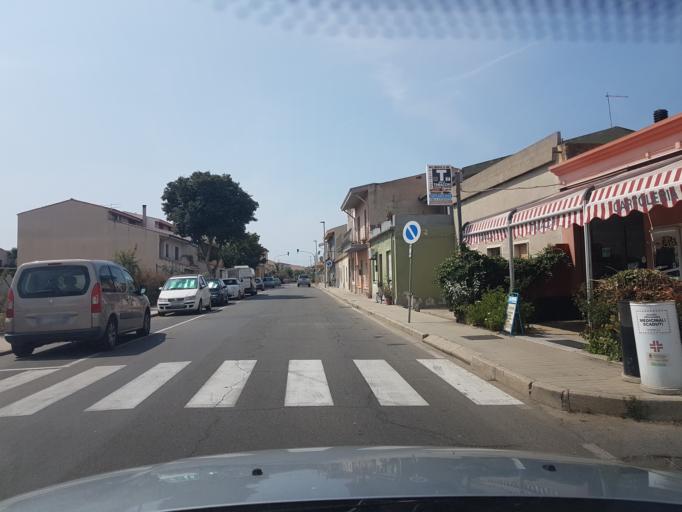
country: IT
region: Sardinia
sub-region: Provincia di Oristano
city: Cabras
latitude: 39.9251
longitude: 8.5374
